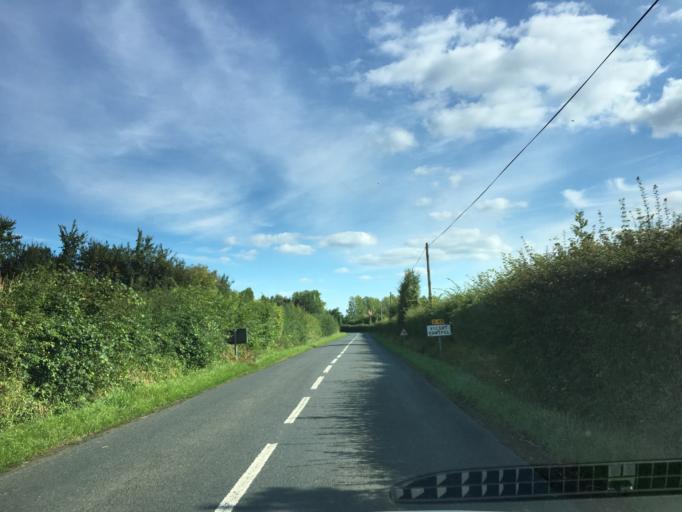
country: FR
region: Lower Normandy
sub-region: Departement du Calvados
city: Cambremer
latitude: 49.1621
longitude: -0.0130
